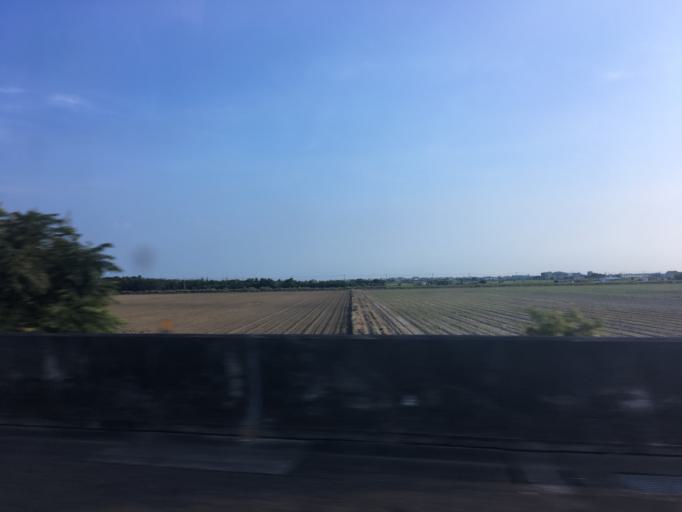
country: TW
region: Taiwan
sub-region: Chiayi
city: Taibao
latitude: 23.4270
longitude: 120.3450
